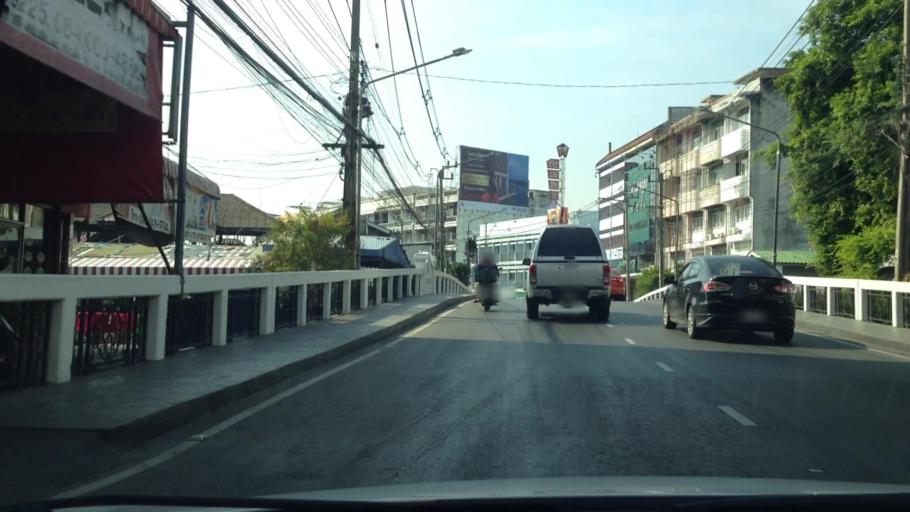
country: TH
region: Samut Prakan
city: Samut Prakan
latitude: 13.5925
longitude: 100.5972
